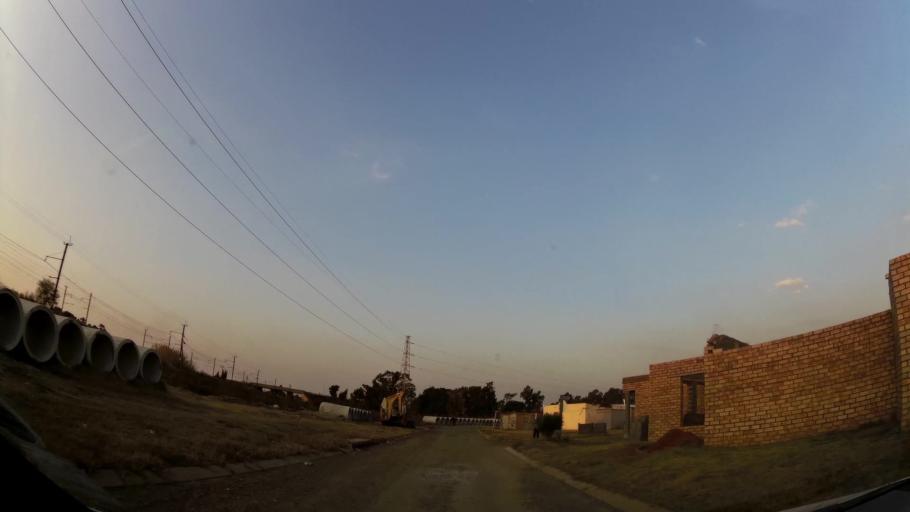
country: ZA
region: Gauteng
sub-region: Ekurhuleni Metropolitan Municipality
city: Springs
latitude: -26.2628
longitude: 28.3925
